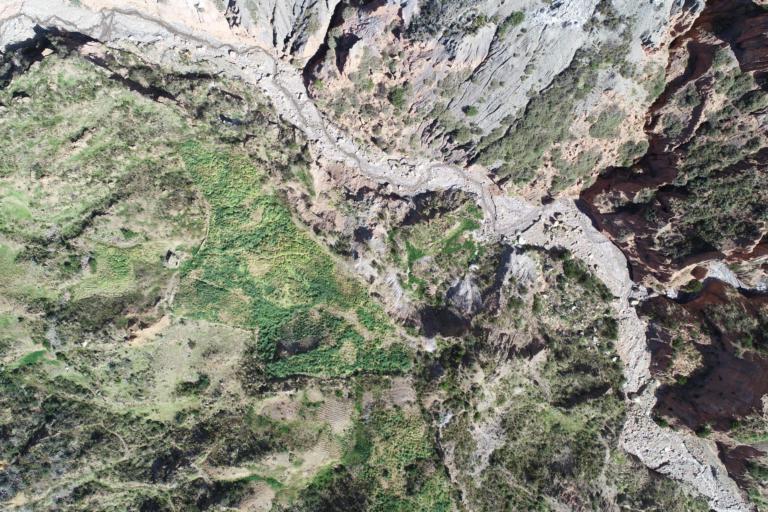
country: BO
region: La Paz
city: La Paz
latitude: -16.5594
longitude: -67.9894
